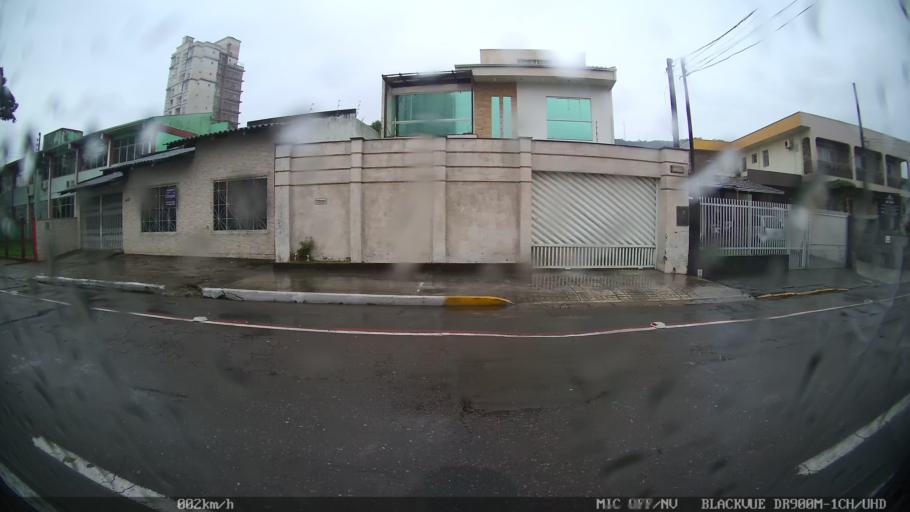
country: BR
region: Santa Catarina
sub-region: Itajai
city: Itajai
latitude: -26.9160
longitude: -48.6709
